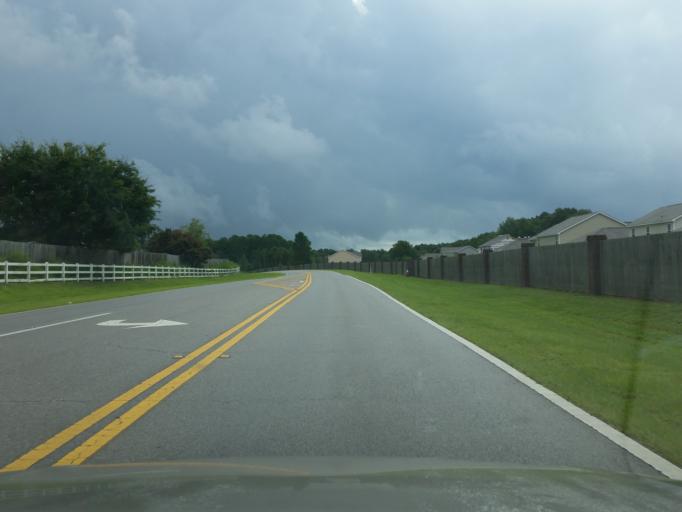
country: US
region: Florida
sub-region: Escambia County
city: West Pensacola
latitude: 30.4467
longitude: -87.2800
